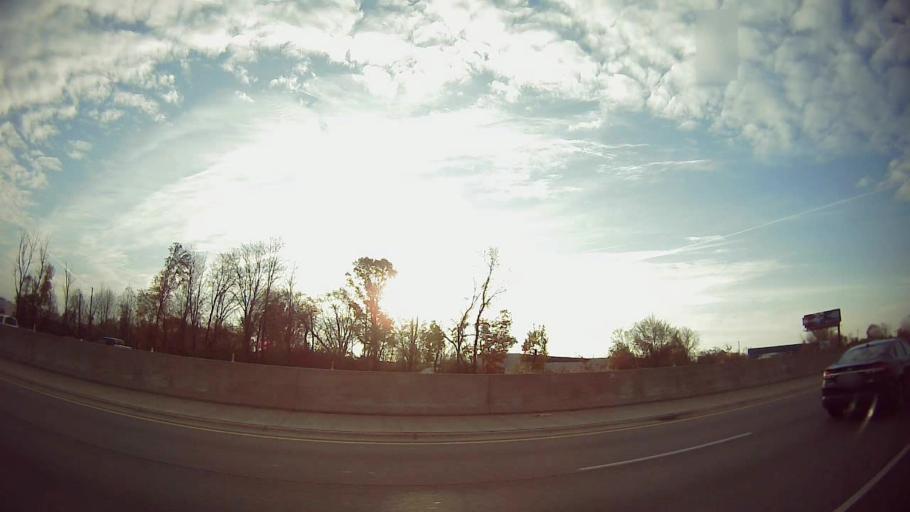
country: US
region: Michigan
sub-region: Macomb County
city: Mount Clemens
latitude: 42.5508
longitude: -82.8771
